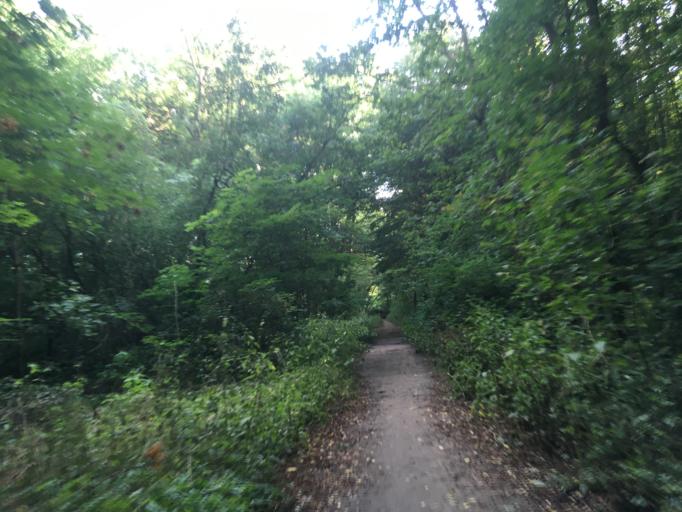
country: DE
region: Berlin
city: Lichtenrade
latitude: 52.3800
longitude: 13.4236
